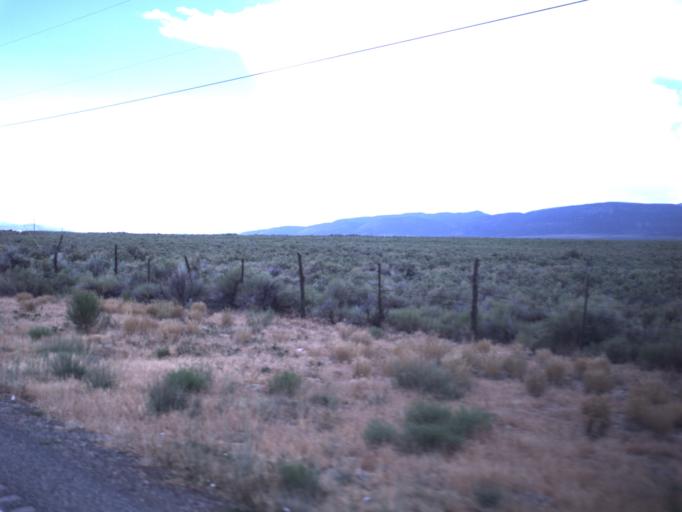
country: US
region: Utah
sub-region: Sanpete County
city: Moroni
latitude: 39.4440
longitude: -111.5625
